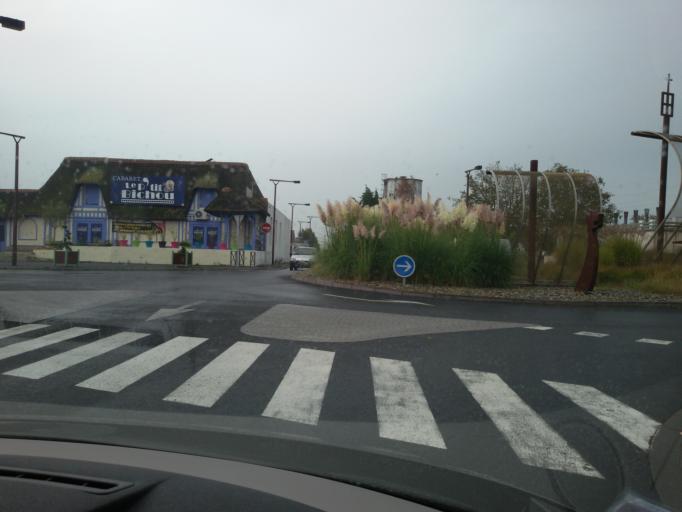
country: FR
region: Lower Normandy
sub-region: Departement du Calvados
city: Cabourg
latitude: 49.2855
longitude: -0.1084
